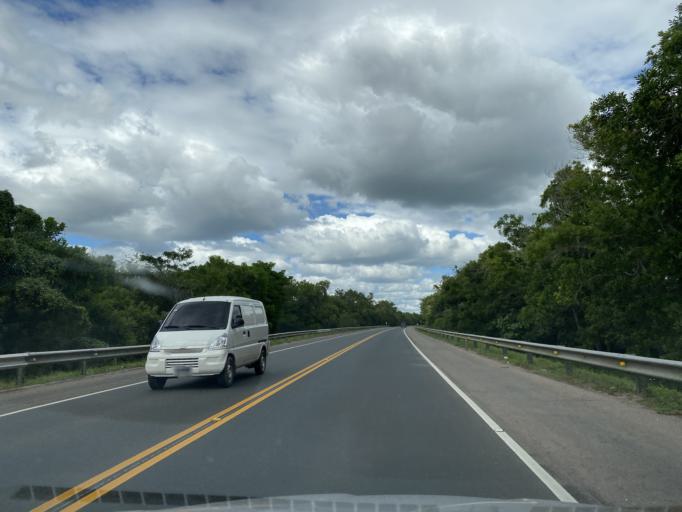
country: DO
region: Santo Domingo
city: Guerra
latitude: 18.6006
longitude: -69.7710
